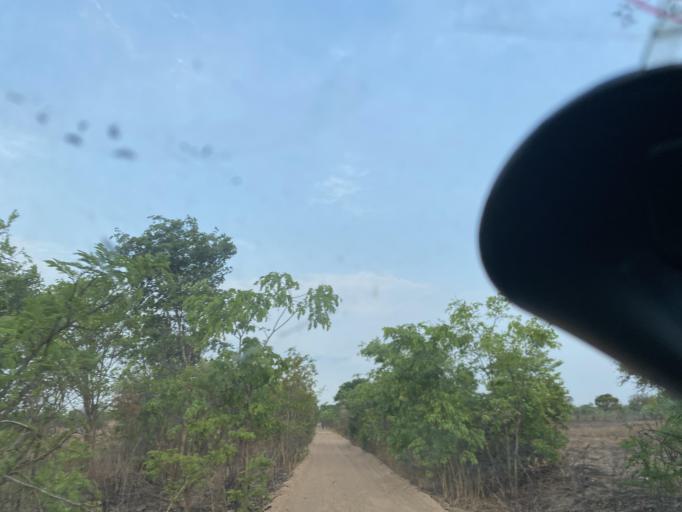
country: ZM
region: Lusaka
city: Chongwe
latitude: -15.2044
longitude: 28.5114
